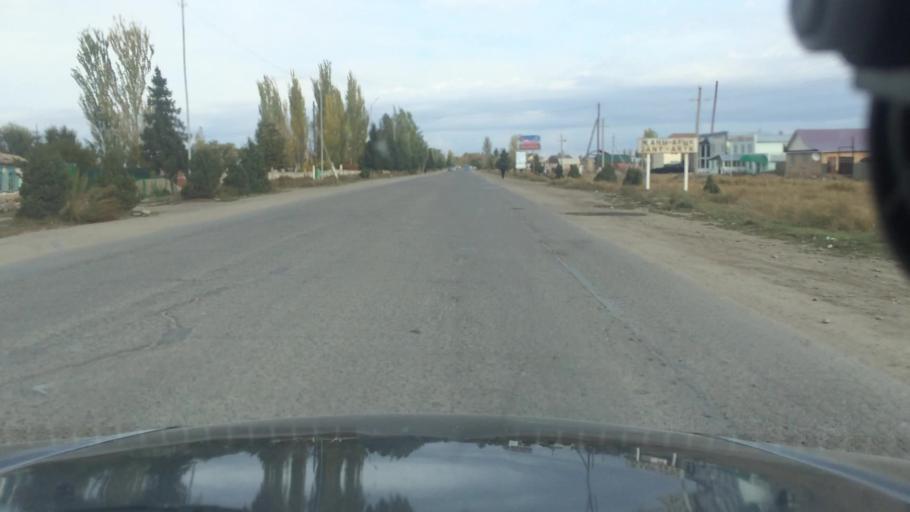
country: KG
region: Ysyk-Koel
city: Karakol
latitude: 42.5241
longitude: 78.3853
